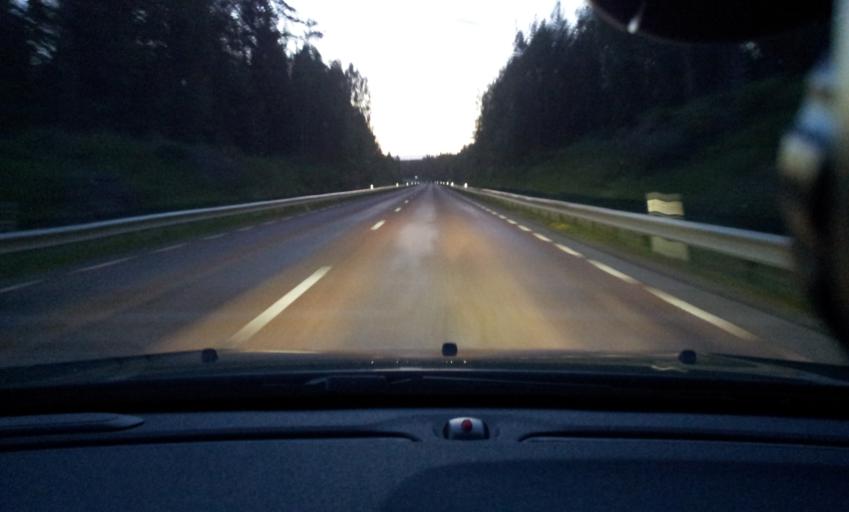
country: SE
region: Jaemtland
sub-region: Bergs Kommun
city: Hoverberg
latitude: 62.8852
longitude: 14.5233
